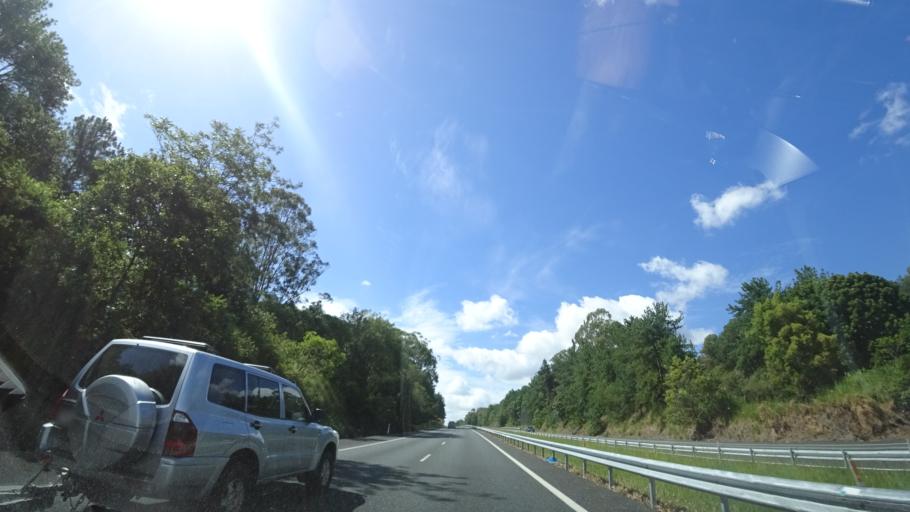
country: AU
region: Queensland
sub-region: Sunshine Coast
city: Woombye
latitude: -26.6617
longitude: 152.9955
